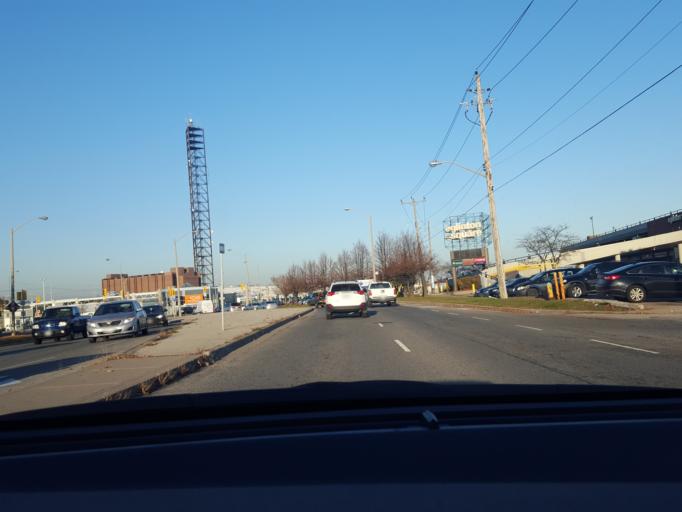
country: CA
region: Ontario
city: Scarborough
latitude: 43.7238
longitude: -79.3013
